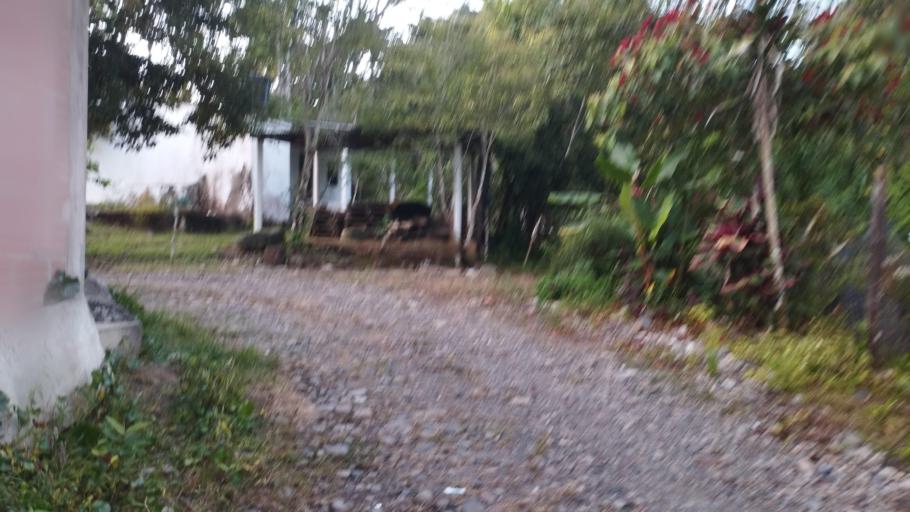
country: CO
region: Boyaca
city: San Luis de Gaceno
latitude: 4.8269
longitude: -73.1644
